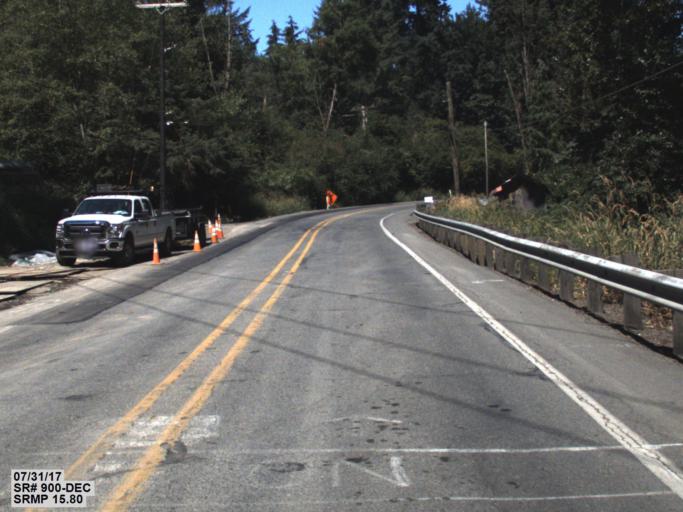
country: US
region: Washington
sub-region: King County
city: East Renton Highlands
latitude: 47.5026
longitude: -122.1295
